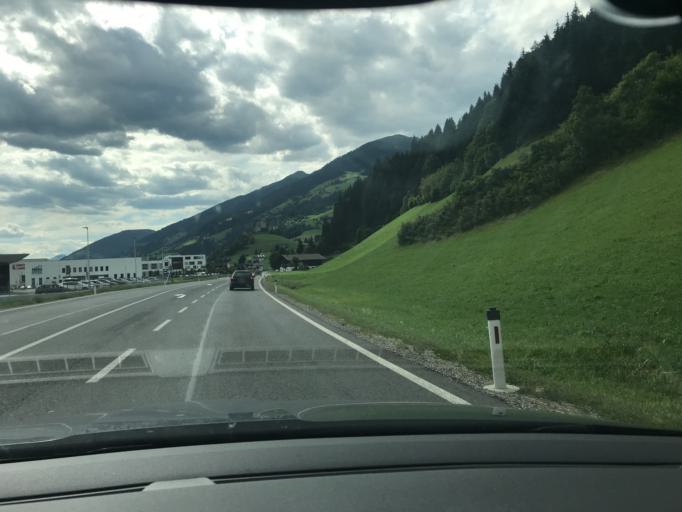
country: AT
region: Tyrol
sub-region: Politischer Bezirk Lienz
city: Heinfels
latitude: 46.7489
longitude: 12.4557
